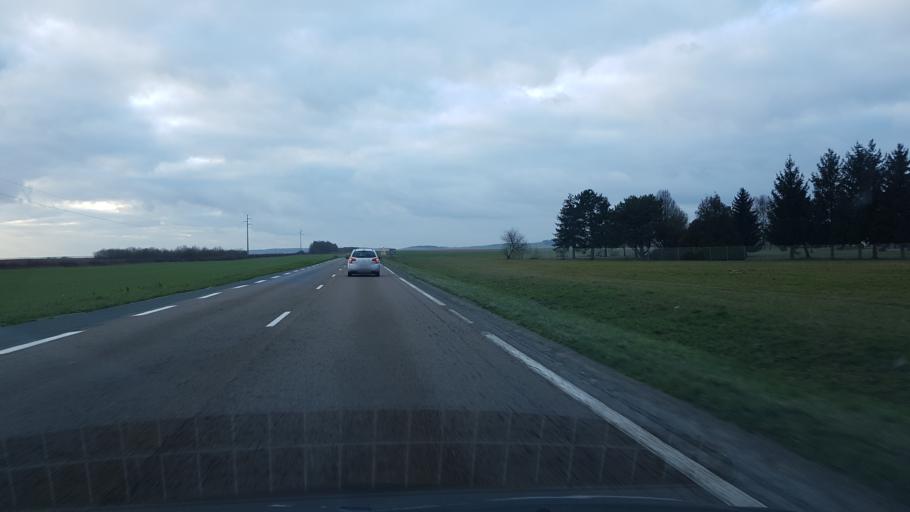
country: FR
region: Champagne-Ardenne
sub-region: Departement de la Marne
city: Connantre
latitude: 48.7253
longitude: 3.8346
